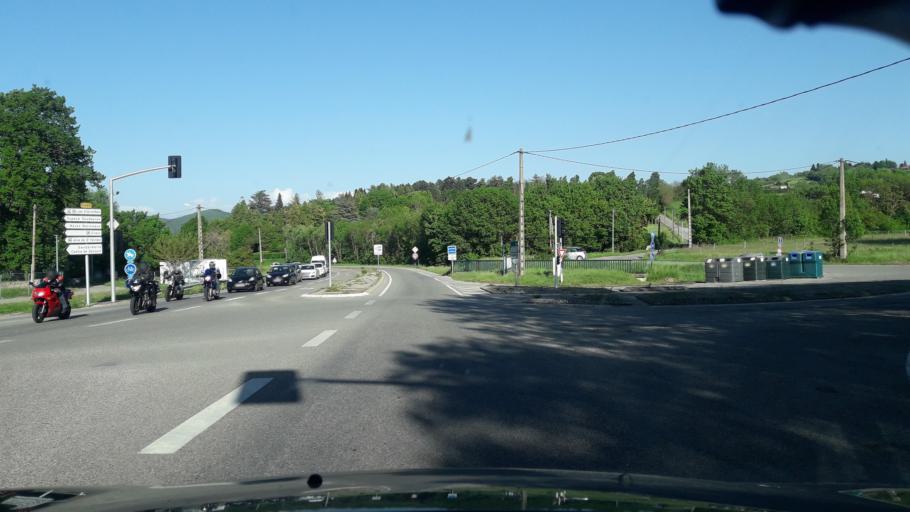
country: FR
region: Rhone-Alpes
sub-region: Departement de la Drome
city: Crest
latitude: 44.7201
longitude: 5.0256
